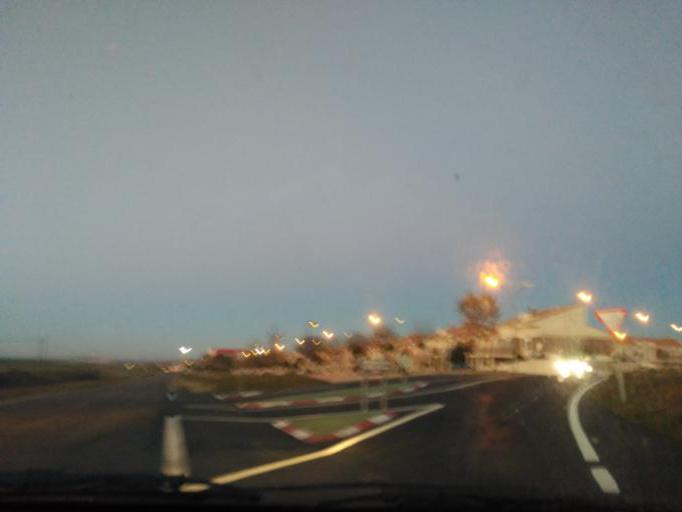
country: ES
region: Castille and Leon
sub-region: Provincia de Salamanca
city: Villares de la Reina
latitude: 41.0065
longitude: -5.6549
